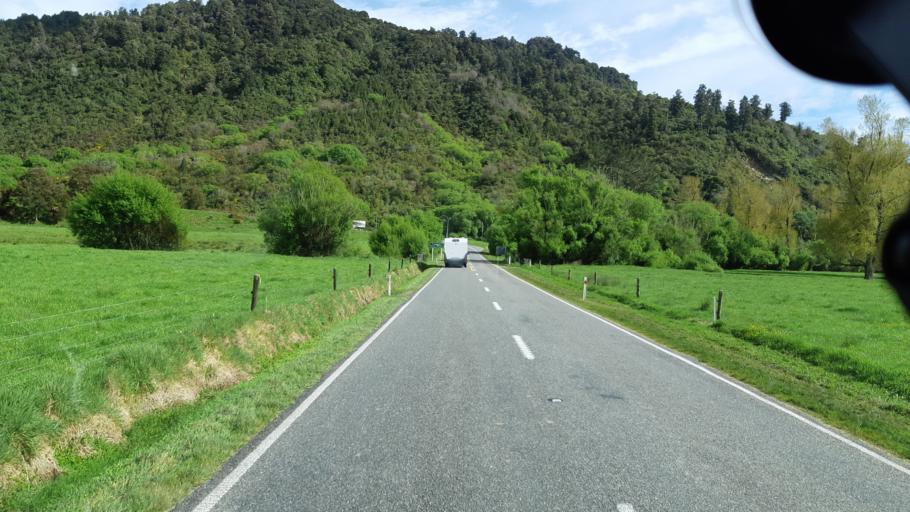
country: NZ
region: West Coast
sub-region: Buller District
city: Westport
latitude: -41.8598
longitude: 171.9394
